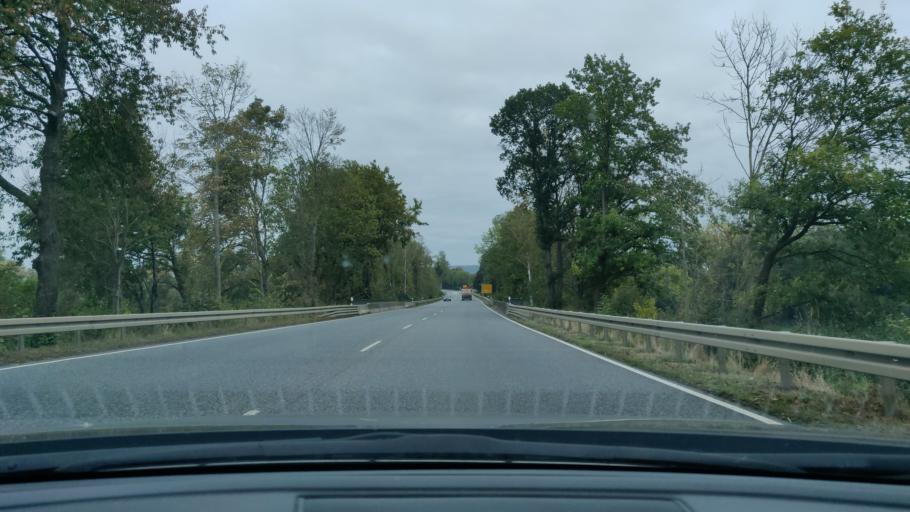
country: DE
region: Hesse
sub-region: Regierungsbezirk Kassel
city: Frielendorf
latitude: 50.9784
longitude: 9.3206
